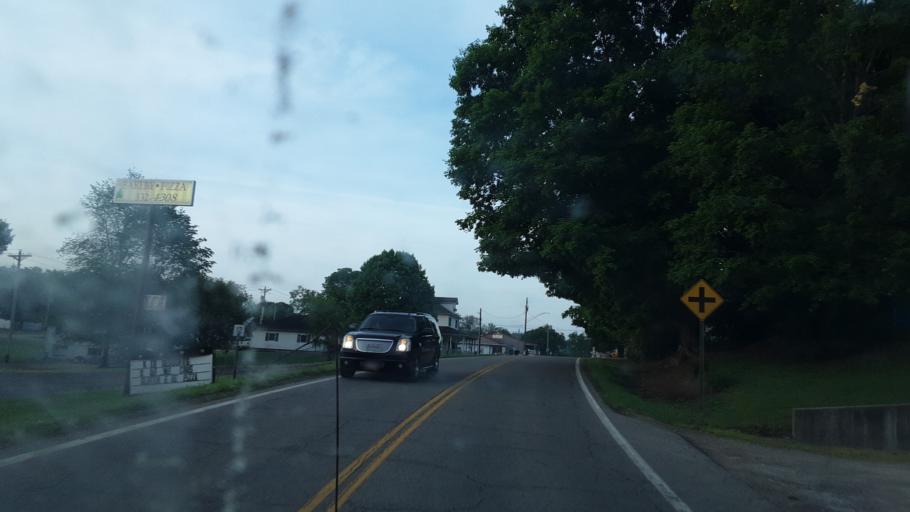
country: US
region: Ohio
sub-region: Ross County
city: Kingston
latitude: 39.4687
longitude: -82.7477
